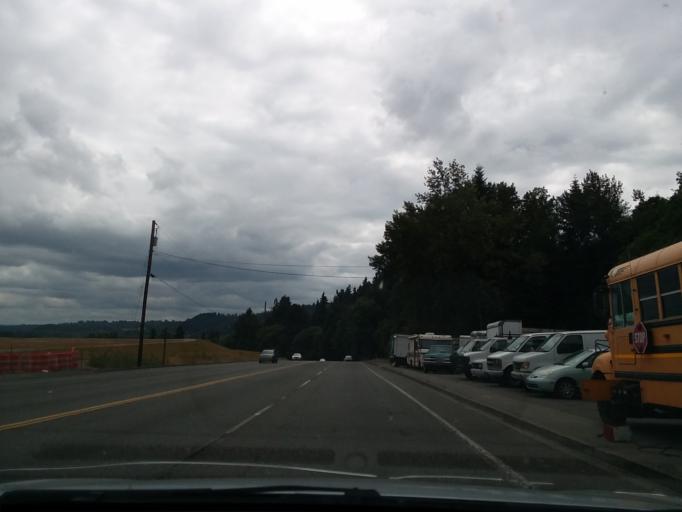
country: US
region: Washington
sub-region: King County
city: SeaTac
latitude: 47.4263
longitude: -122.2758
